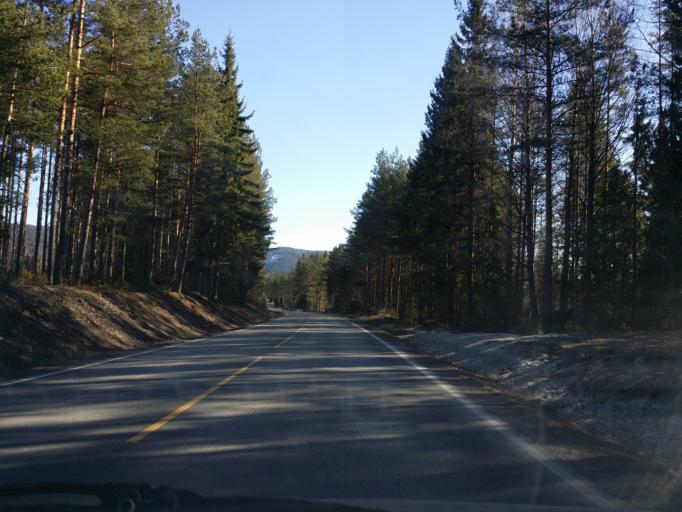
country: NO
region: Buskerud
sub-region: Ringerike
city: Honefoss
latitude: 60.3058
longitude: 10.1637
